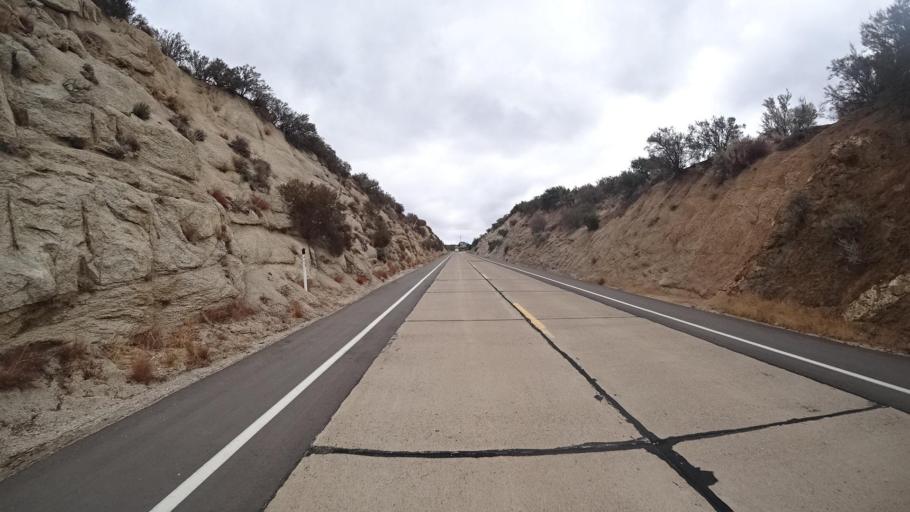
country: US
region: California
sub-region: San Diego County
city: Campo
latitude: 32.7255
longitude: -116.4210
